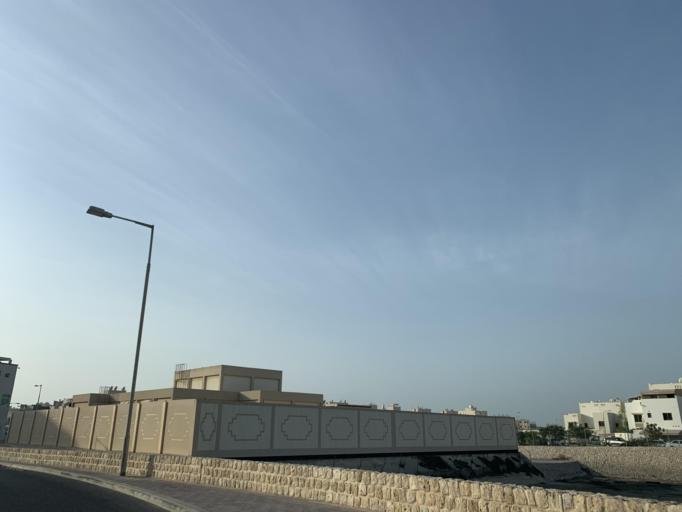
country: BH
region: Central Governorate
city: Madinat Hamad
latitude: 26.1220
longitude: 50.4894
